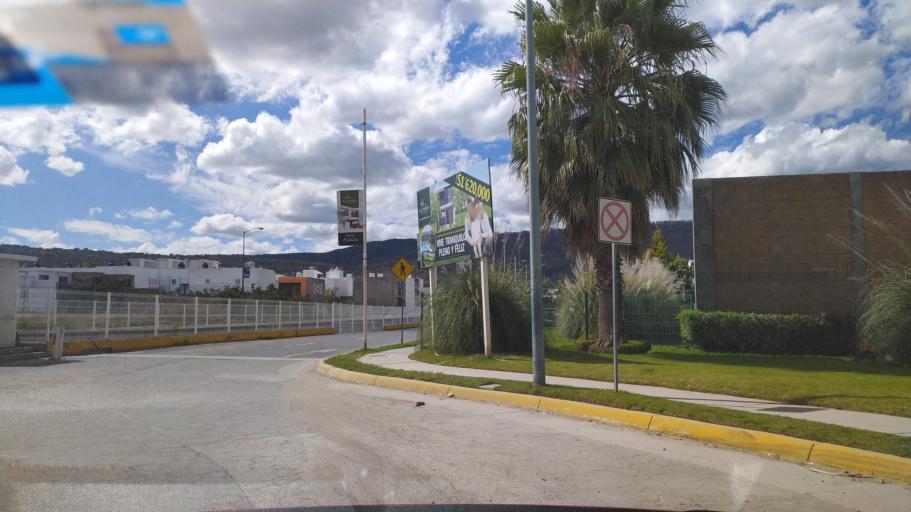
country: MX
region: Jalisco
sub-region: Tlajomulco de Zuniga
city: Palomar
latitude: 20.6313
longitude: -103.4769
